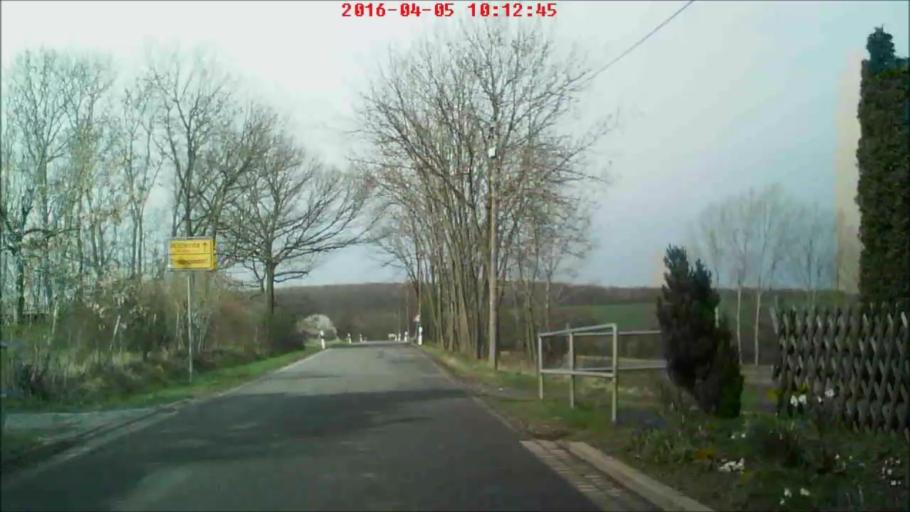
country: DE
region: Thuringia
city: Witterda
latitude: 51.0252
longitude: 10.9116
